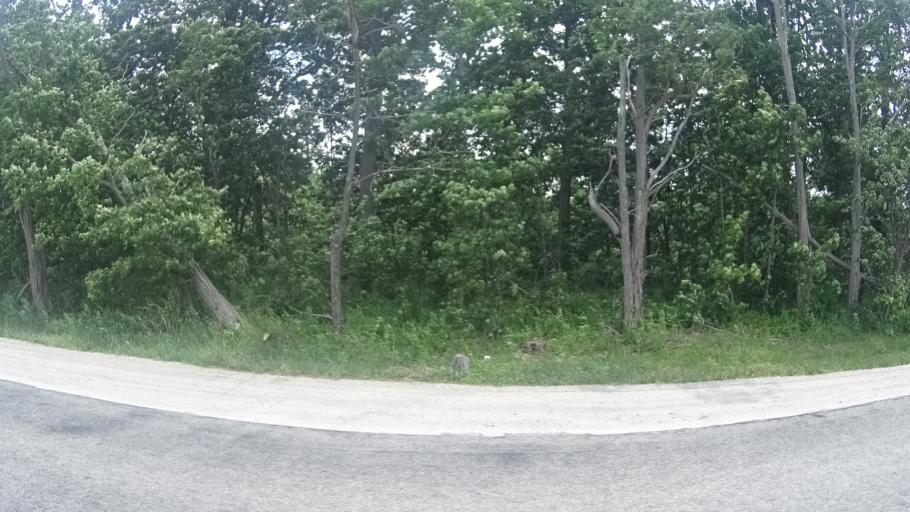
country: US
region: Ohio
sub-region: Huron County
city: Monroeville
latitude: 41.2901
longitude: -82.6745
